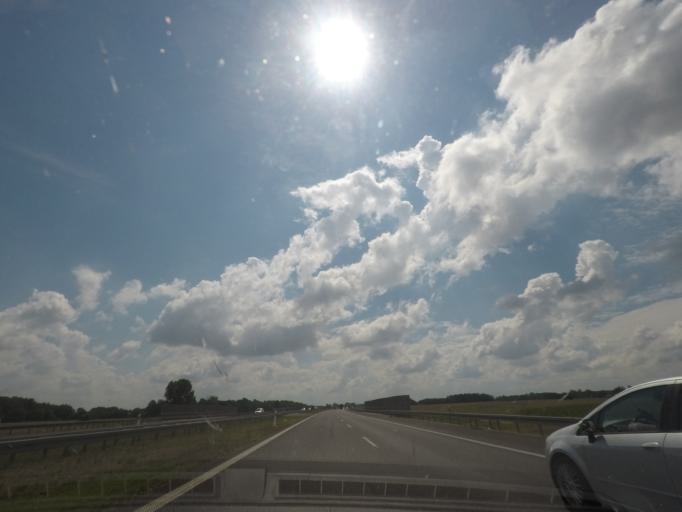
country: PL
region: Lodz Voivodeship
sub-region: Powiat zgierski
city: Strykow
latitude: 51.9506
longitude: 19.6036
